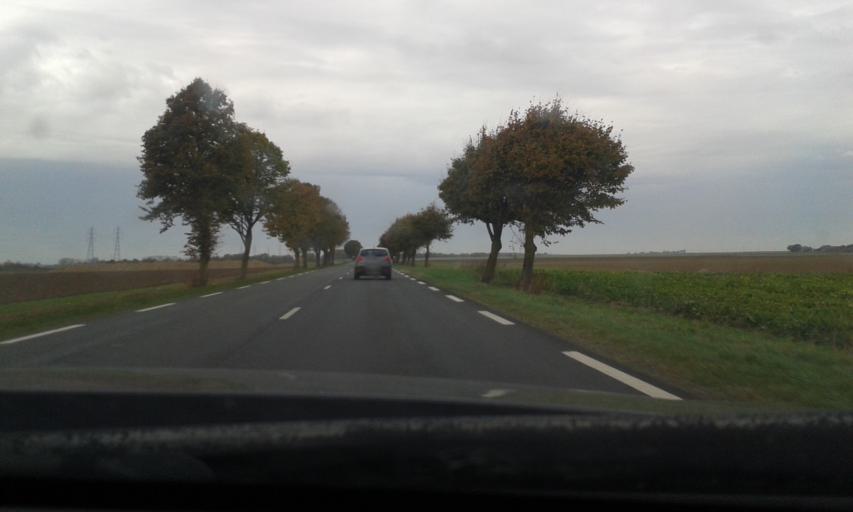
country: FR
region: Centre
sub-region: Departement du Loiret
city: Artenay
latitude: 48.1188
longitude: 1.8586
